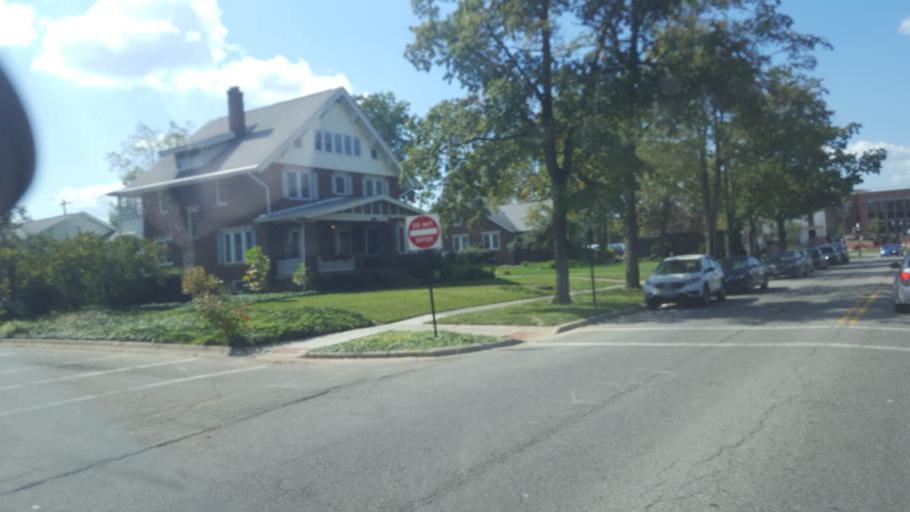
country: US
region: Ohio
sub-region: Franklin County
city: Grove City
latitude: 39.8826
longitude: -83.0909
